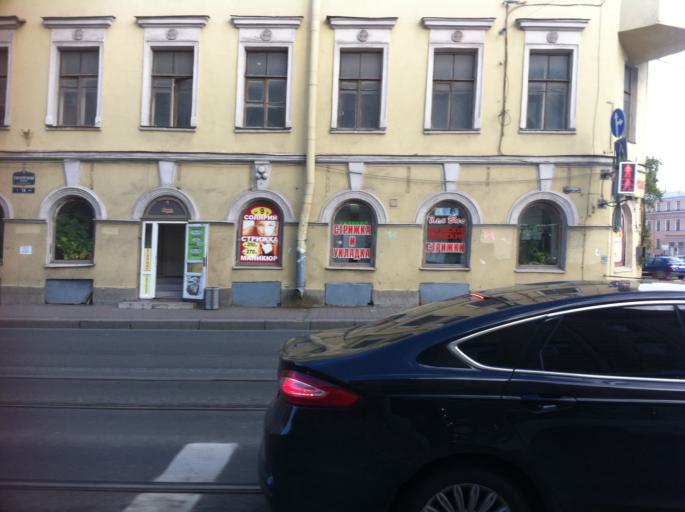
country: RU
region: St.-Petersburg
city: Admiralteisky
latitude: 59.9097
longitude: 30.2754
